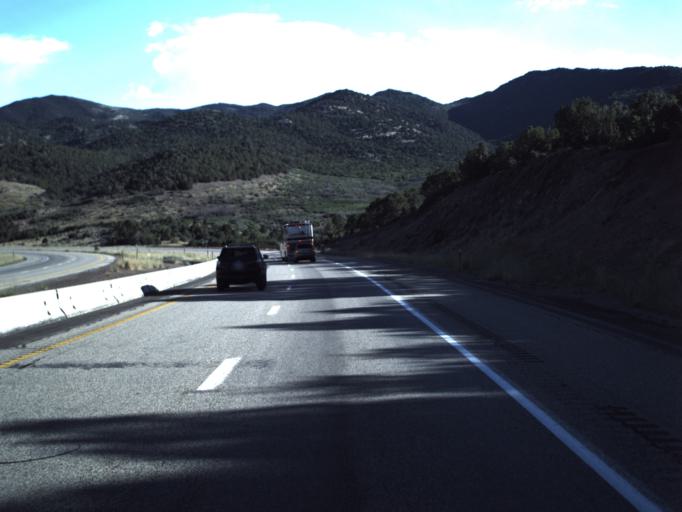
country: US
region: Utah
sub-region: Beaver County
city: Beaver
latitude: 38.6014
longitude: -112.5067
